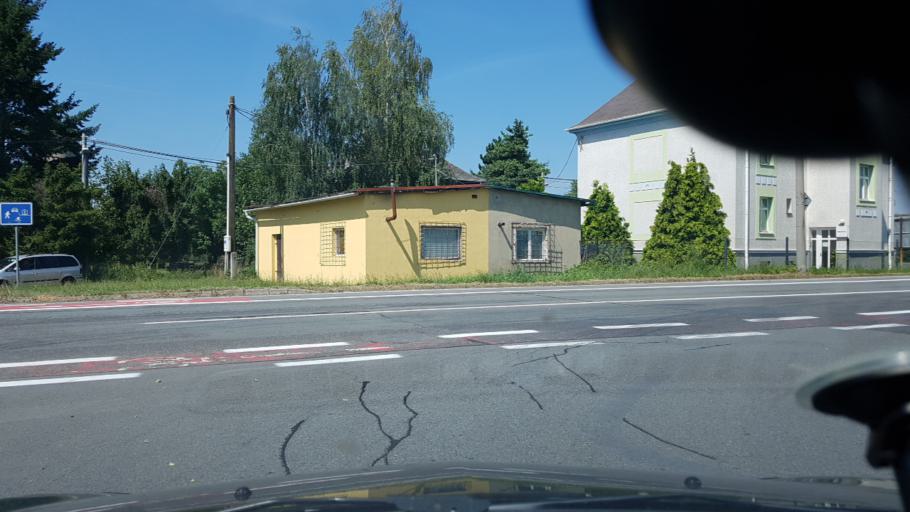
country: CZ
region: Moravskoslezsky
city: Stary Bohumin
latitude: 49.8964
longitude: 18.3329
